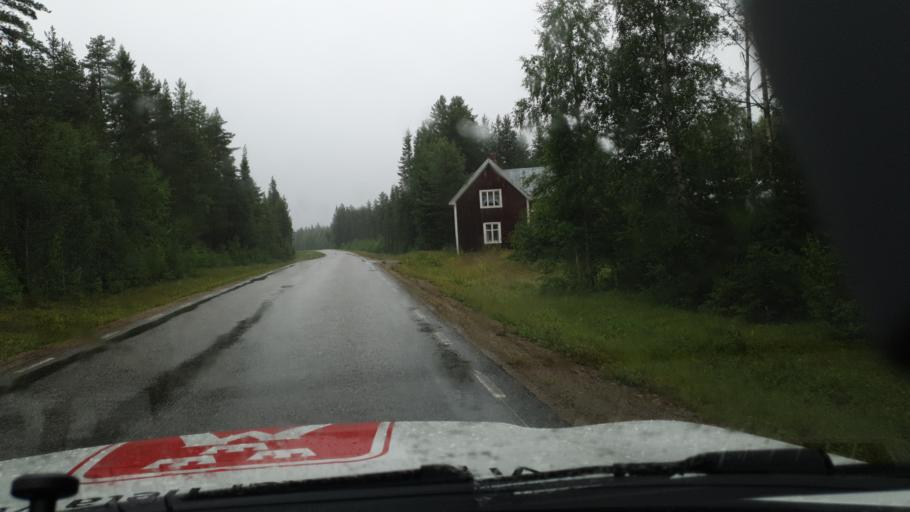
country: SE
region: Vaesterbotten
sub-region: Skelleftea Kommun
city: Langsele
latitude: 64.6326
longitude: 19.9848
